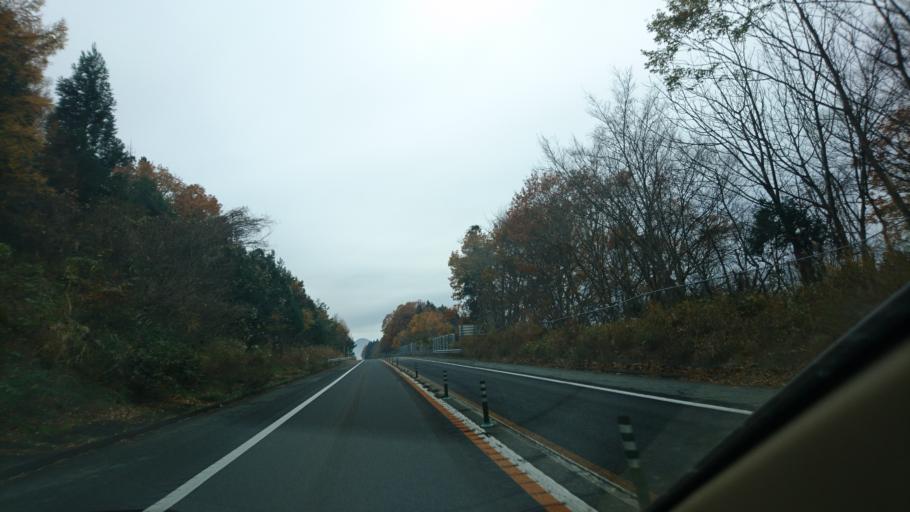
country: JP
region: Iwate
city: Kitakami
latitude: 39.2805
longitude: 141.0338
